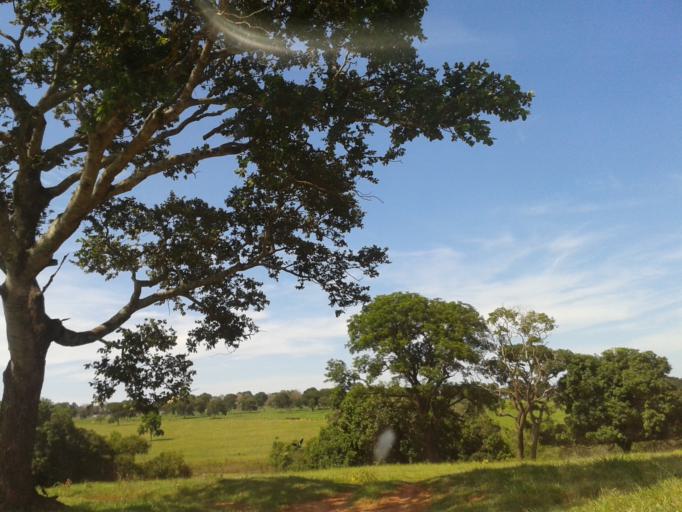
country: BR
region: Minas Gerais
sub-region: Santa Vitoria
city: Santa Vitoria
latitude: -19.1681
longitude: -50.5221
